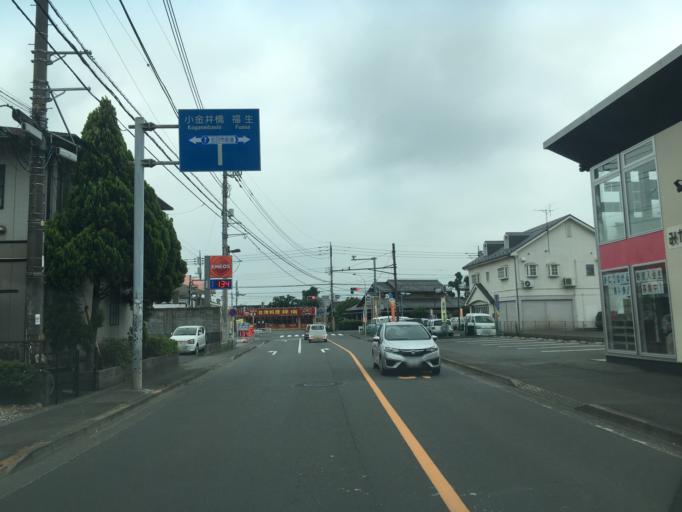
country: JP
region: Tokyo
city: Hino
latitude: 35.7254
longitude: 139.3997
